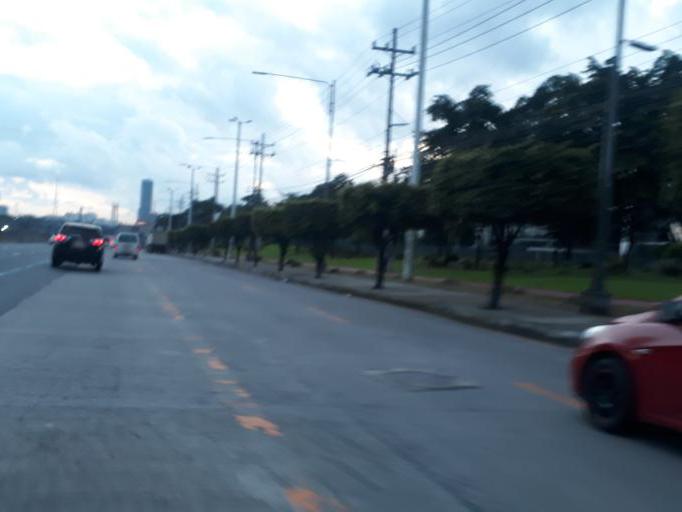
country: PH
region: Metro Manila
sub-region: Quezon City
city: Quezon City
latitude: 14.6588
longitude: 121.0601
